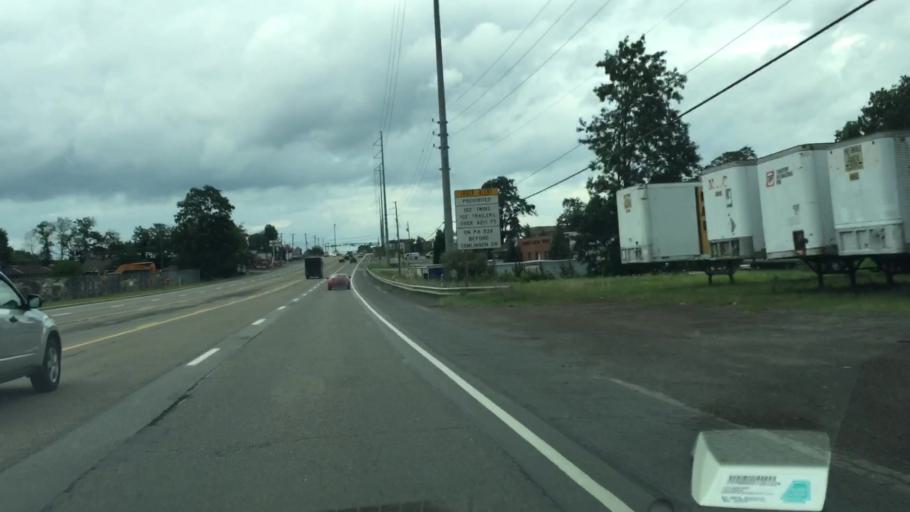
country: US
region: Pennsylvania
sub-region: Butler County
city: Zelienople
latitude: 40.7485
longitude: -80.1149
